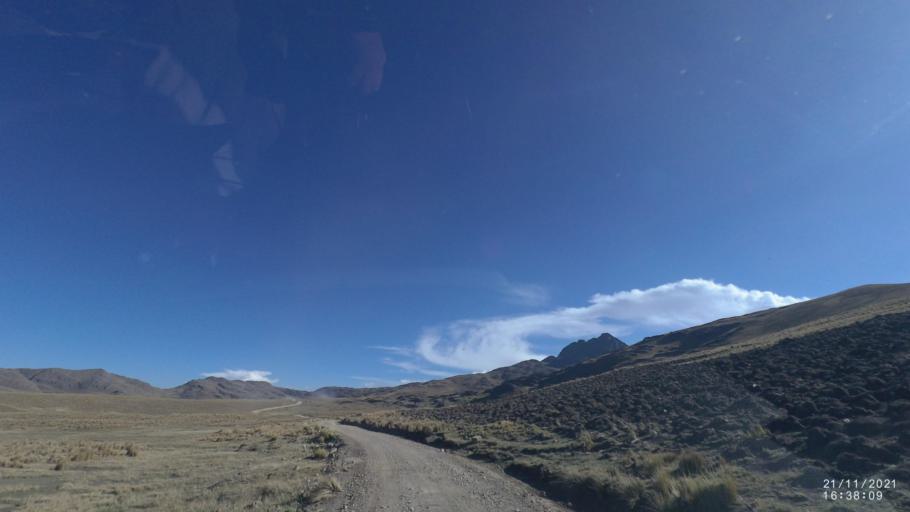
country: BO
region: Cochabamba
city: Cochabamba
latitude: -17.0496
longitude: -66.2631
